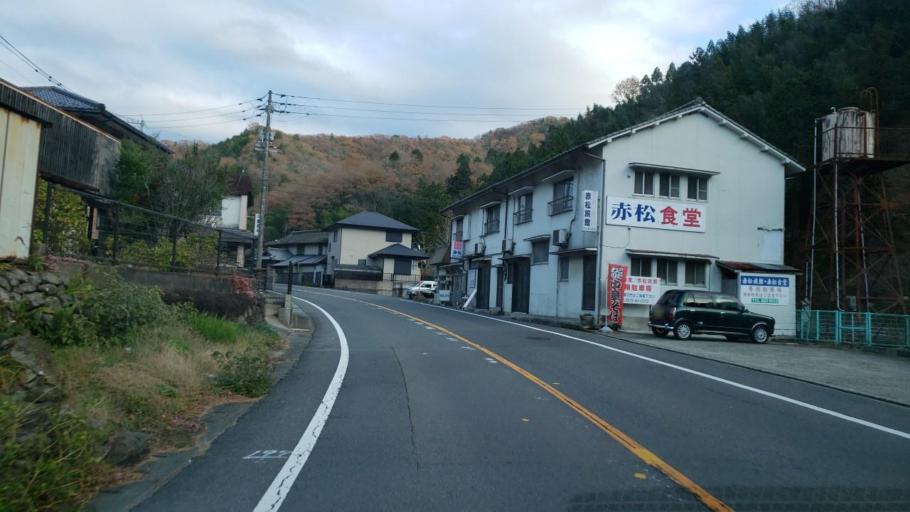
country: JP
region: Tokushima
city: Wakimachi
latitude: 34.1685
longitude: 134.0857
